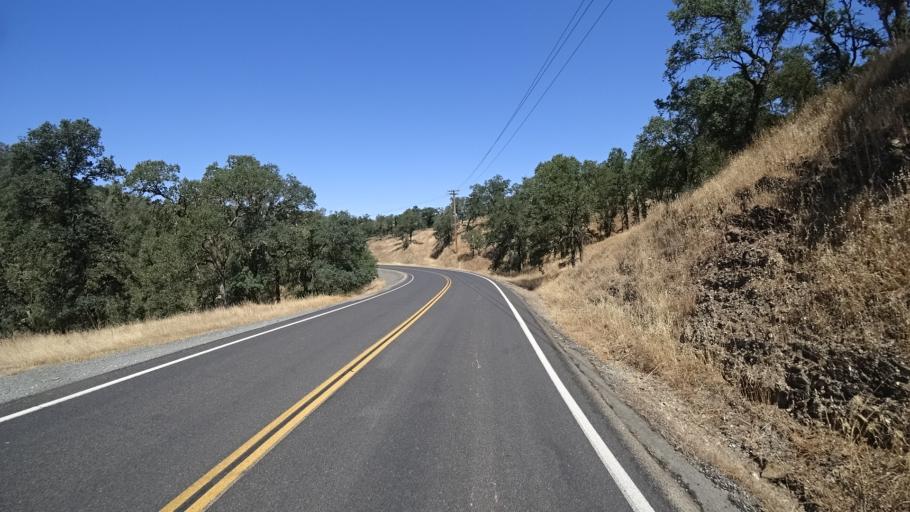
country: US
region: California
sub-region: Calaveras County
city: Copperopolis
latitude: 37.9359
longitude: -120.6308
